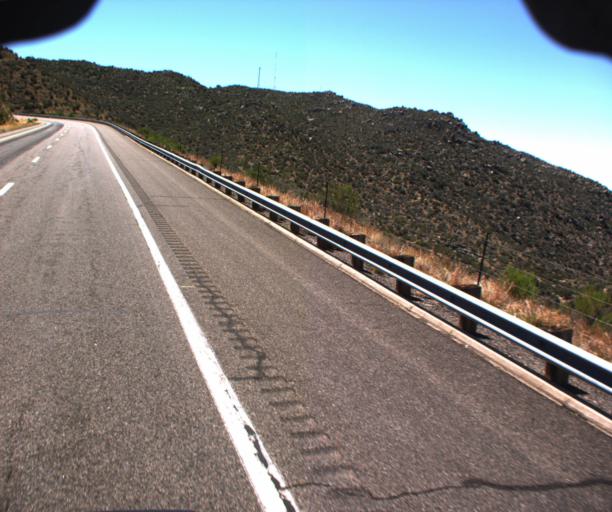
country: US
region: Arizona
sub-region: Yavapai County
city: Congress
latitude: 34.2035
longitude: -112.7595
